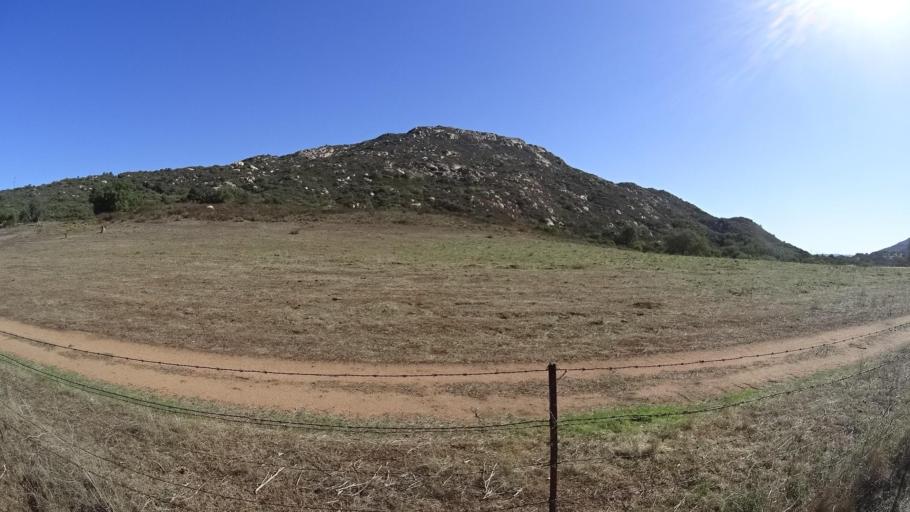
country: US
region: California
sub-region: San Diego County
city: Alpine
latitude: 32.7164
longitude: -116.7561
